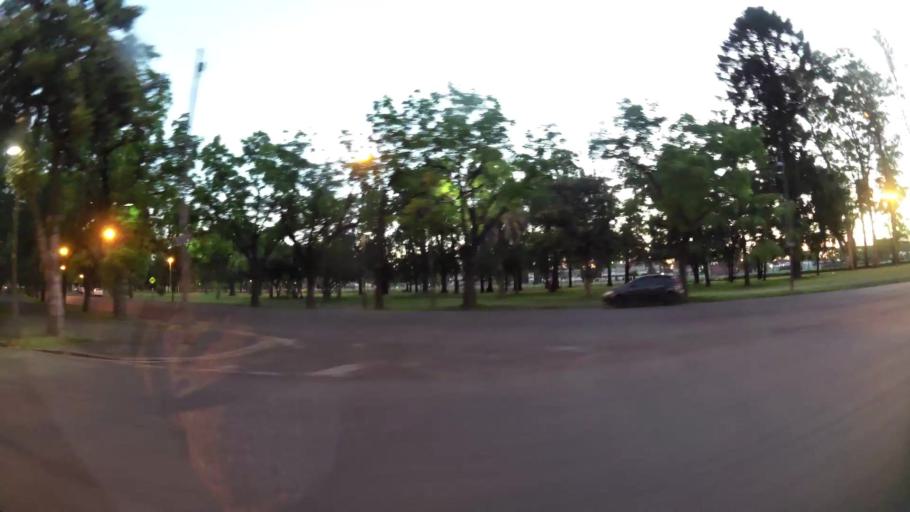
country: AR
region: Santa Fe
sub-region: Departamento de Rosario
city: Rosario
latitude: -32.9585
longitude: -60.6591
